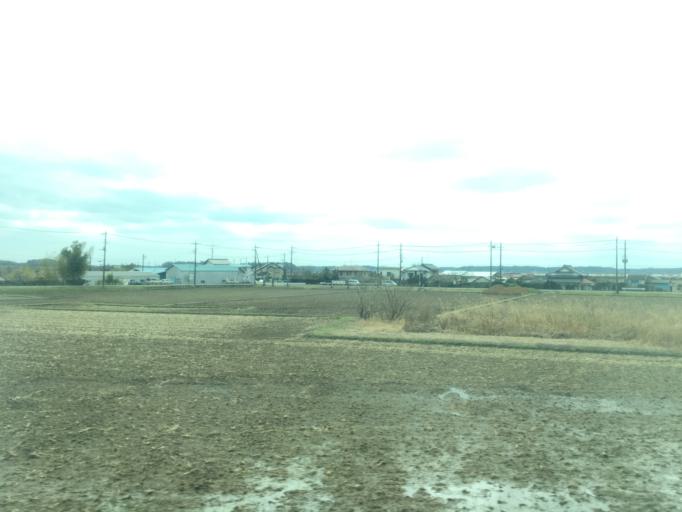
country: JP
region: Chiba
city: Narita
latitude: 35.8097
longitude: 140.2745
